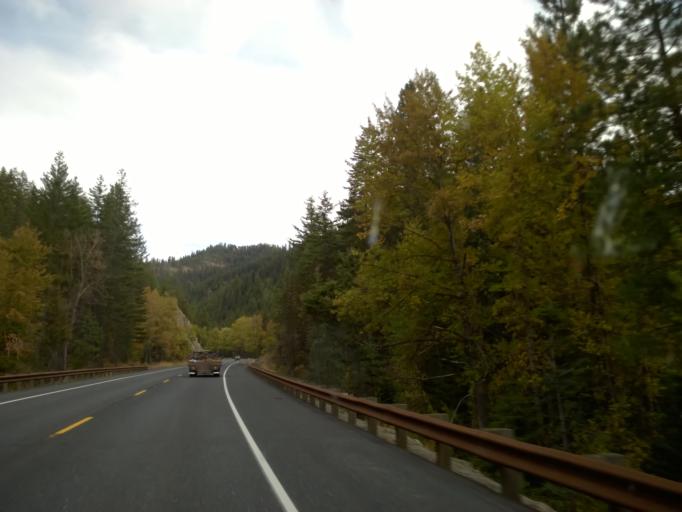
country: US
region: Washington
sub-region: Chelan County
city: Leavenworth
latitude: 47.3991
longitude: -120.6520
